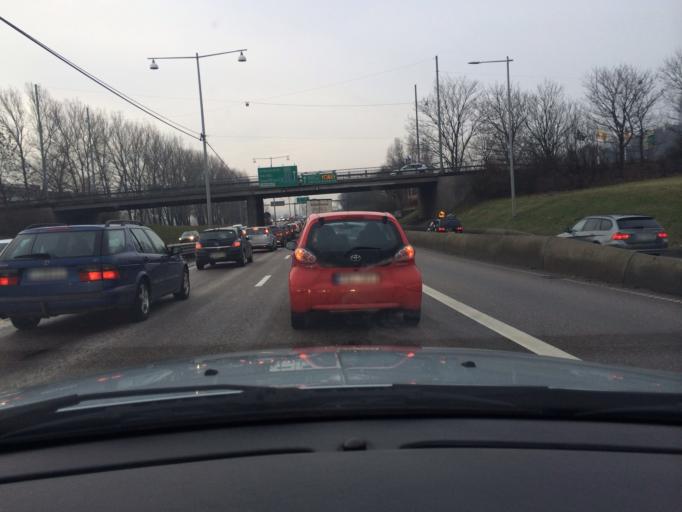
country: SE
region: Vaestra Goetaland
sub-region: Goteborg
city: Goeteborg
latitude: 57.7314
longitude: 11.9838
